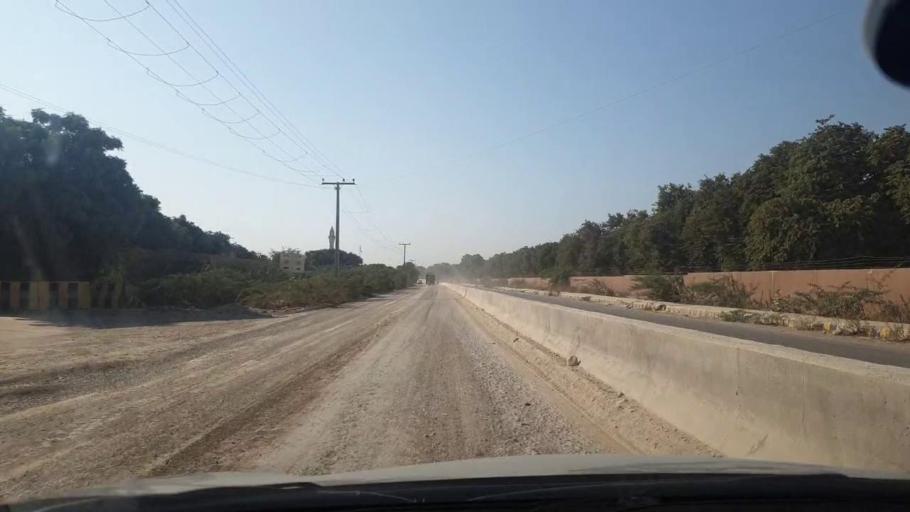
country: PK
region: Sindh
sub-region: Karachi District
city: Karachi
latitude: 25.0905
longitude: 67.0133
